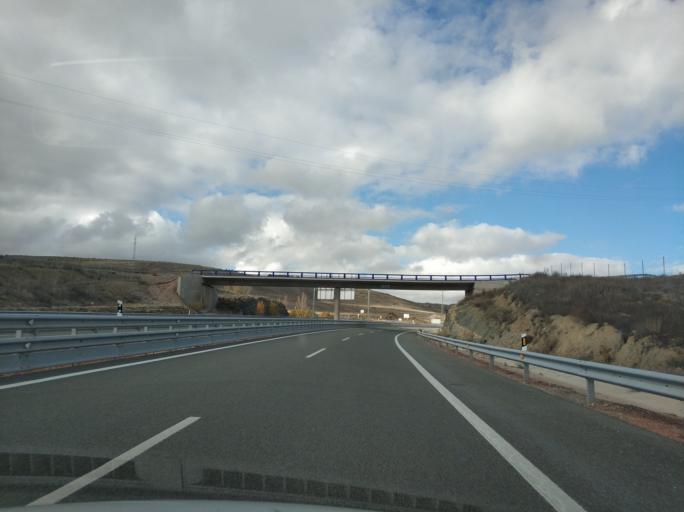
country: ES
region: Castille and Leon
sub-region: Provincia de Soria
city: Medinaceli
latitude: 41.1827
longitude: -2.4296
